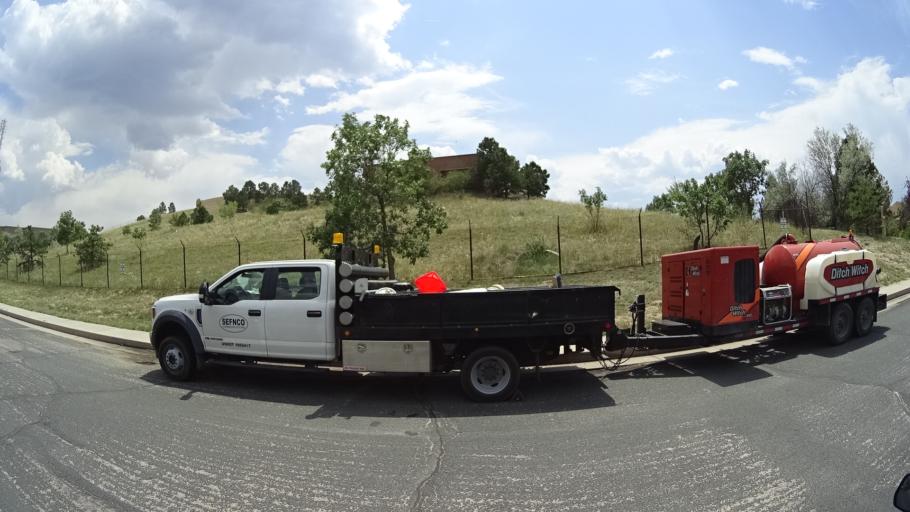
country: US
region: Colorado
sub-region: El Paso County
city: Black Forest
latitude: 38.9593
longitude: -104.7693
